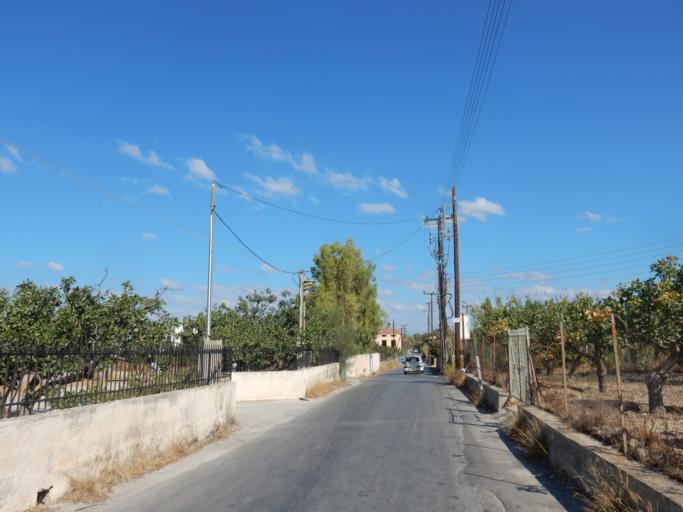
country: GR
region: Attica
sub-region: Nomos Piraios
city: Aegina
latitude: 37.7391
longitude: 23.4367
